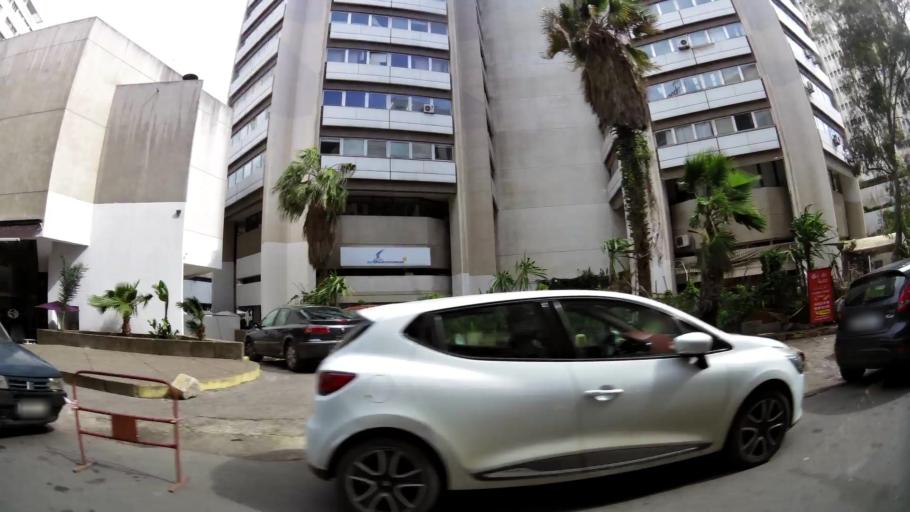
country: MA
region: Grand Casablanca
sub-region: Casablanca
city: Casablanca
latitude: 33.5960
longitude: -7.6128
